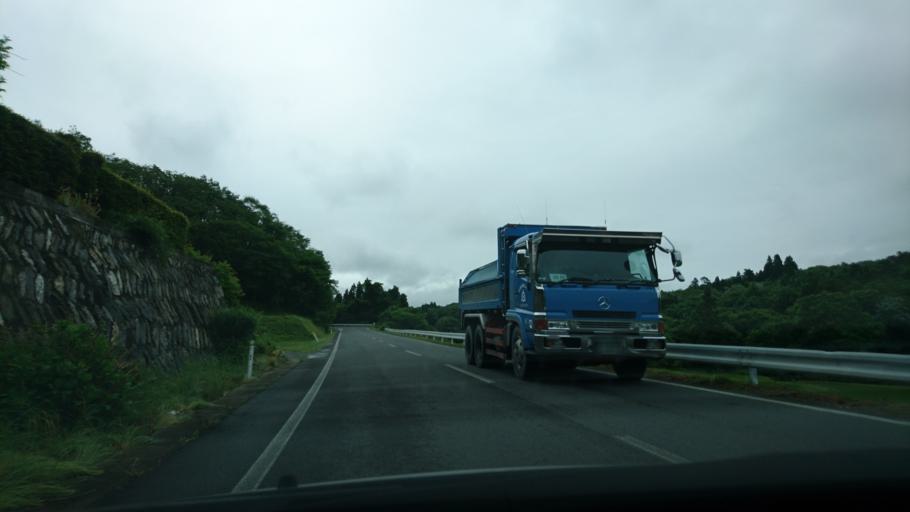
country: JP
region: Iwate
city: Ichinoseki
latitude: 38.9002
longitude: 141.1660
